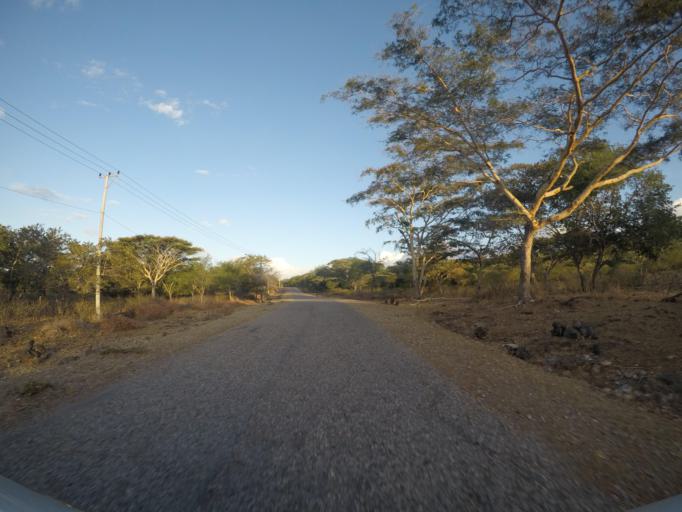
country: TL
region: Lautem
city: Lospalos
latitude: -8.3285
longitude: 126.9994
